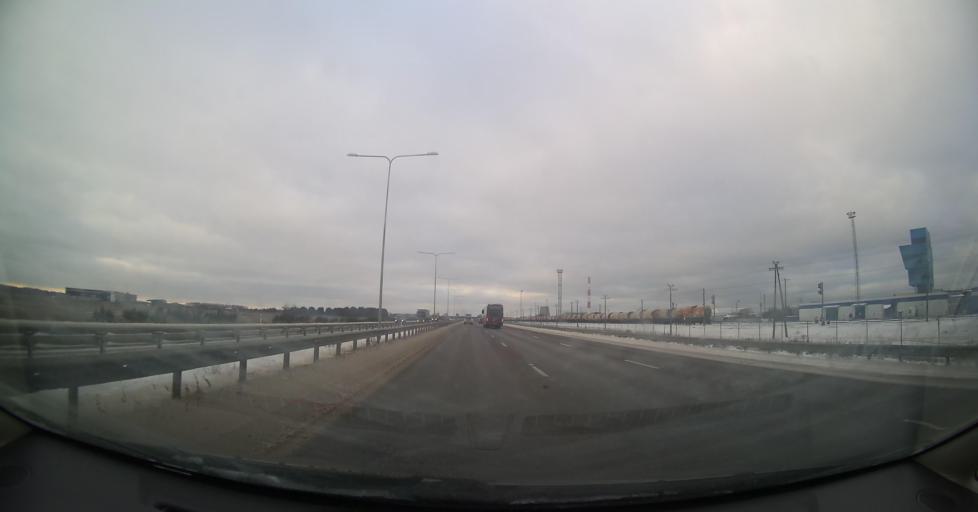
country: EE
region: Harju
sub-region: Joelaehtme vald
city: Loo
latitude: 59.4530
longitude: 24.9776
